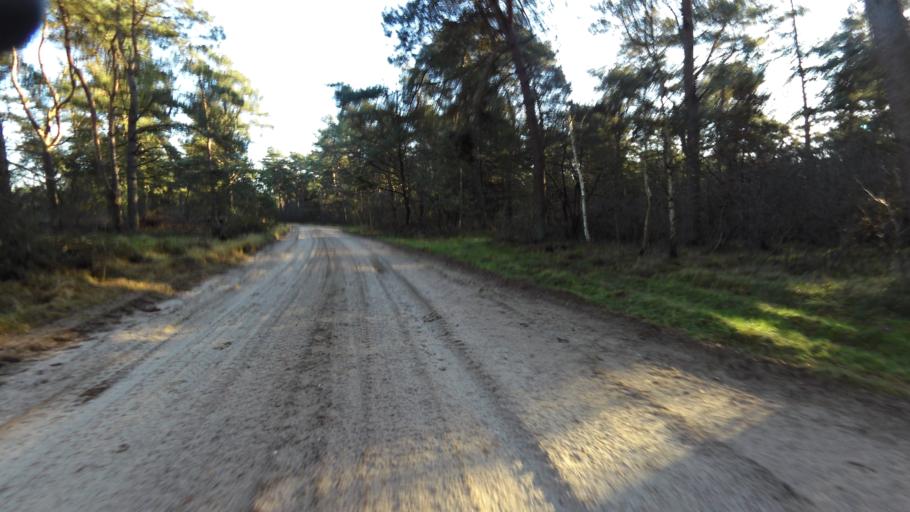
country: NL
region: Gelderland
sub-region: Gemeente Barneveld
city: Garderen
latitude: 52.2075
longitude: 5.7310
